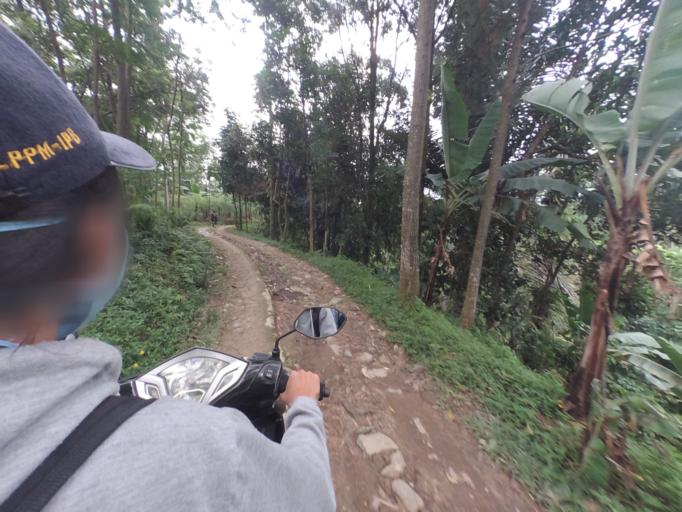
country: ID
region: West Java
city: Cicurug
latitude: -6.7025
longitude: 106.6622
